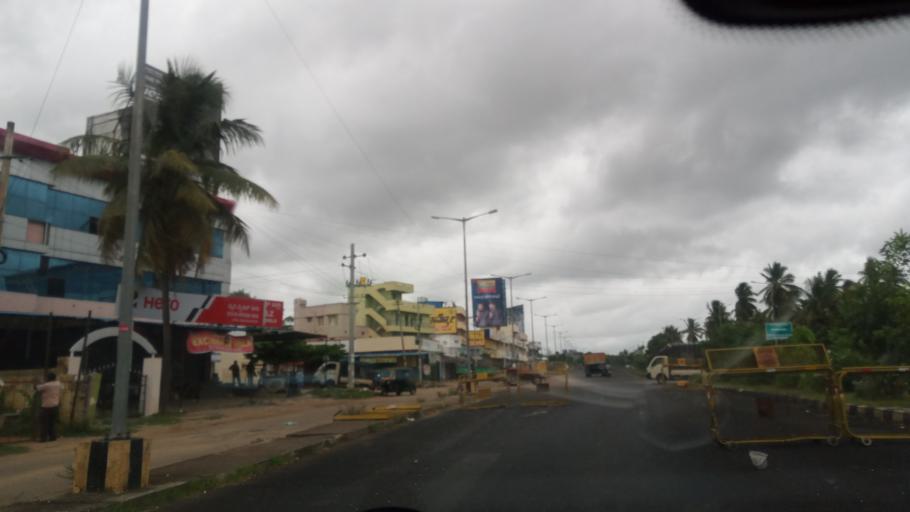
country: IN
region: Karnataka
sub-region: Mysore
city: Mysore
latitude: 12.2945
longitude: 76.6042
